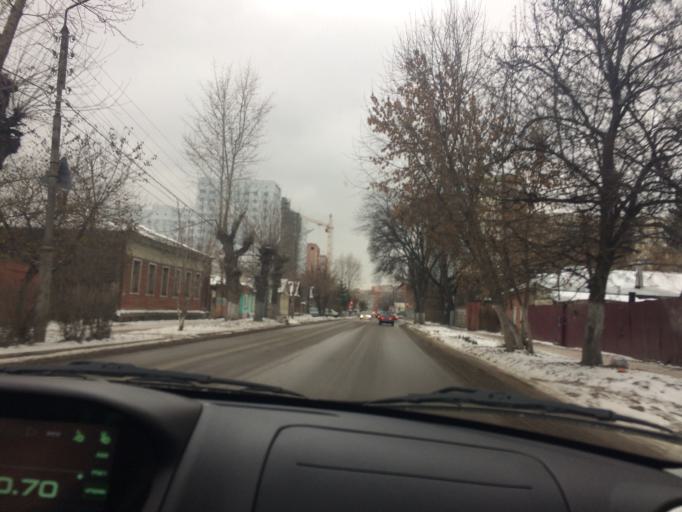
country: RU
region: Rjazan
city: Ryazan'
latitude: 54.6228
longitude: 39.7364
